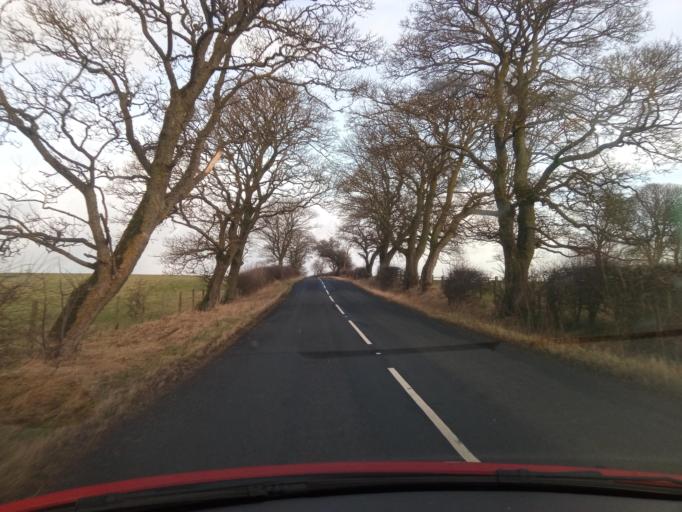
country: GB
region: England
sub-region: Northumberland
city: Acomb
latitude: 55.0876
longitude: -2.0621
